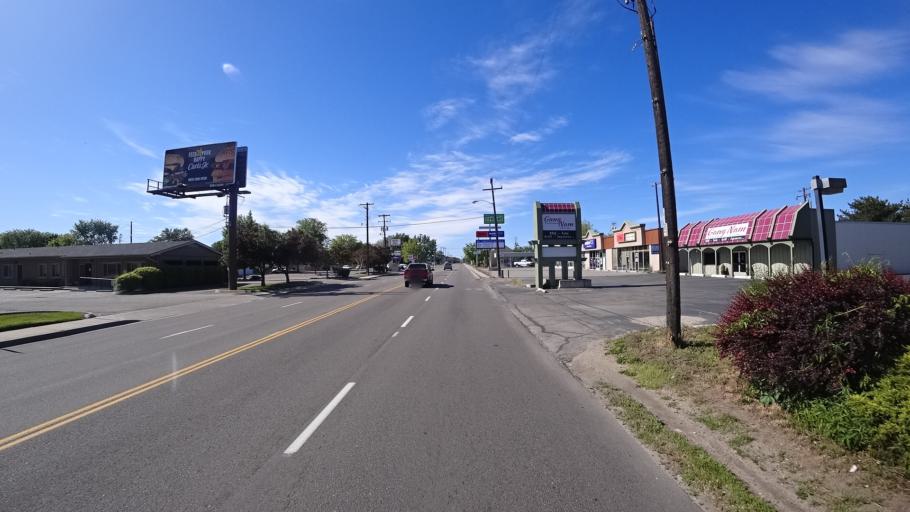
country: US
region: Idaho
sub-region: Ada County
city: Garden City
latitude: 43.6074
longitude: -116.2435
